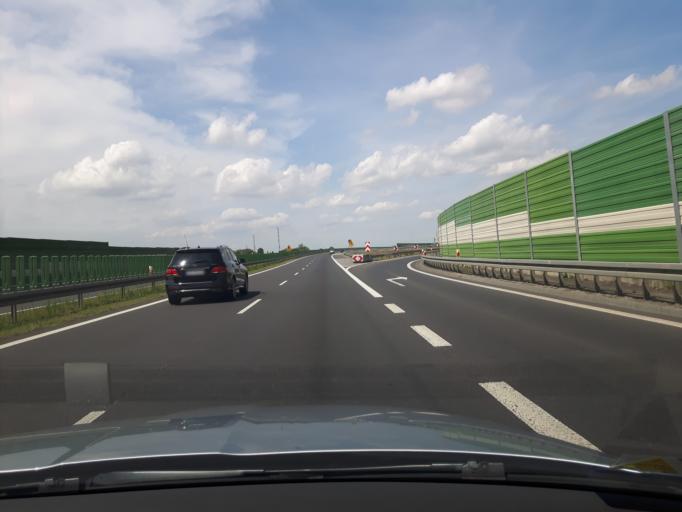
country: PL
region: Masovian Voivodeship
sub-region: Powiat plonski
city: Plonsk
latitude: 52.6107
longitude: 20.3925
